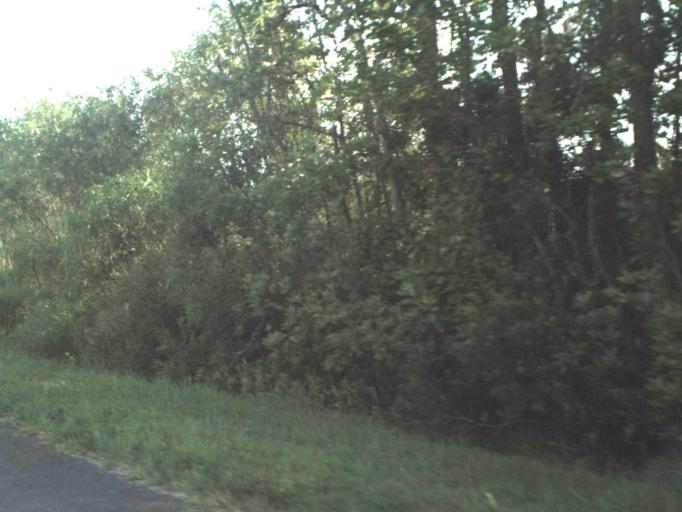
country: US
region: Florida
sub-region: Lake County
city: Groveland
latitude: 28.5034
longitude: -81.8379
